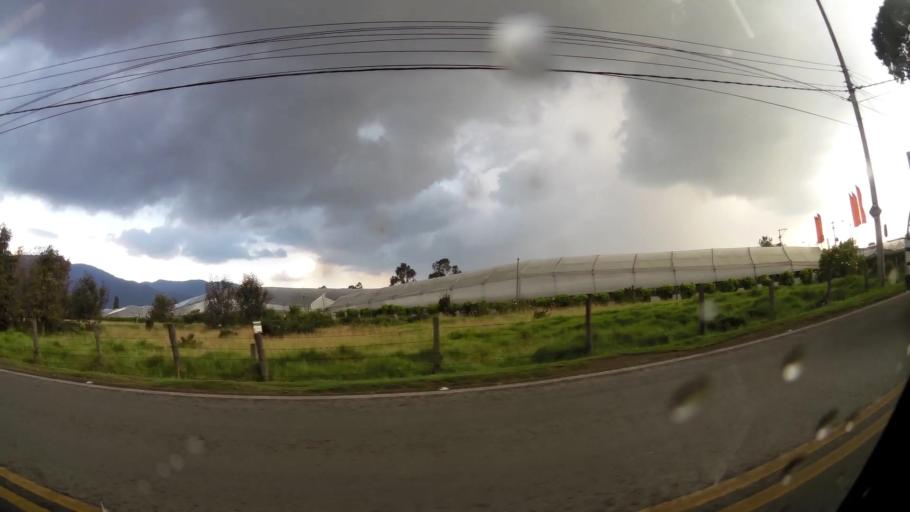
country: CO
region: Cundinamarca
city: Chia
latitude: 4.8482
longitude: -74.0527
